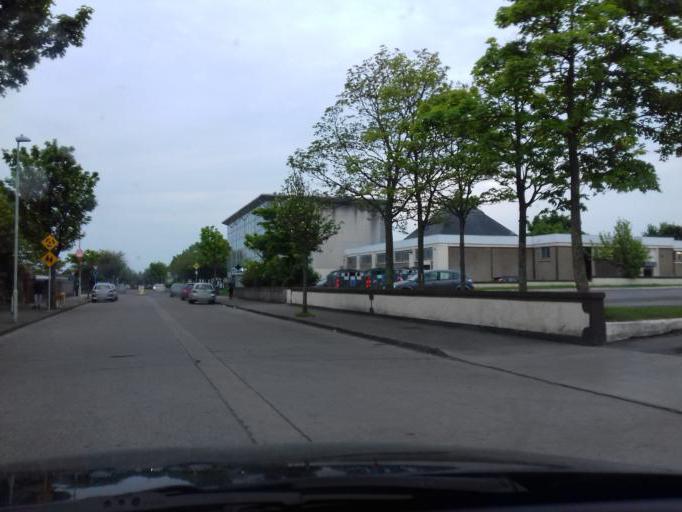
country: IE
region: Leinster
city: Donaghmede
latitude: 53.3859
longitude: -6.1548
